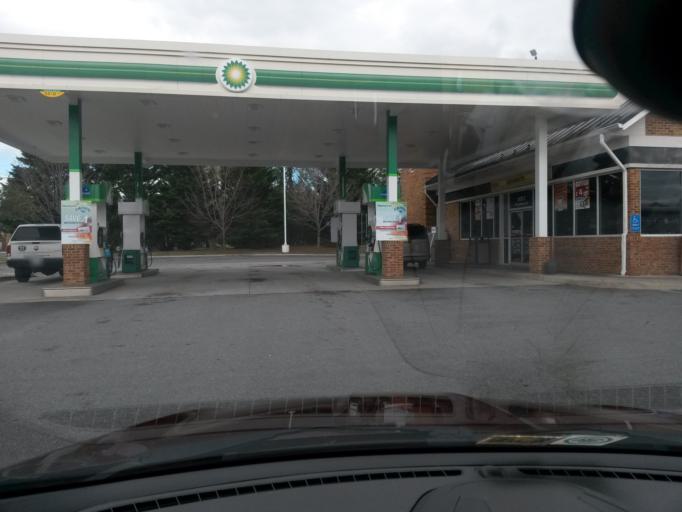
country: US
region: Virginia
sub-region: Bedford County
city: Forest
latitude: 37.4487
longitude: -79.2604
